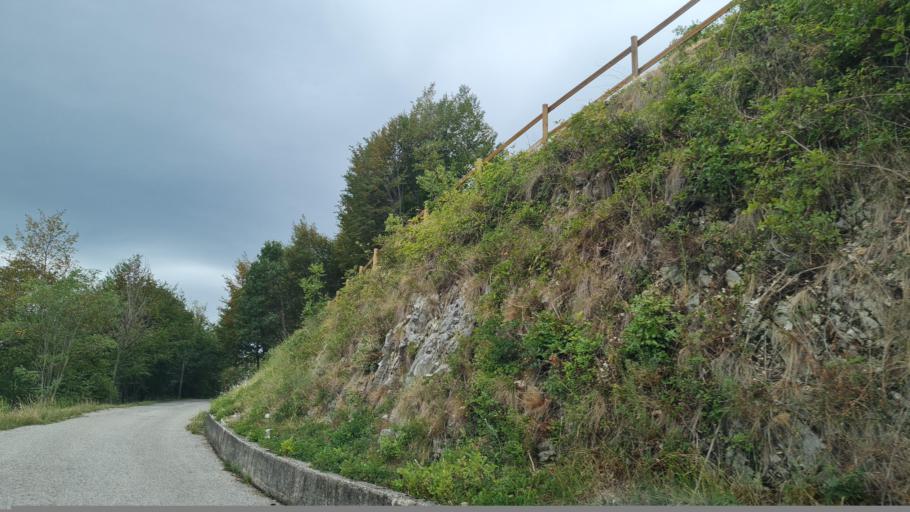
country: IT
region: Veneto
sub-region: Provincia di Vicenza
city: Marostica
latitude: 45.7880
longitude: 11.6645
